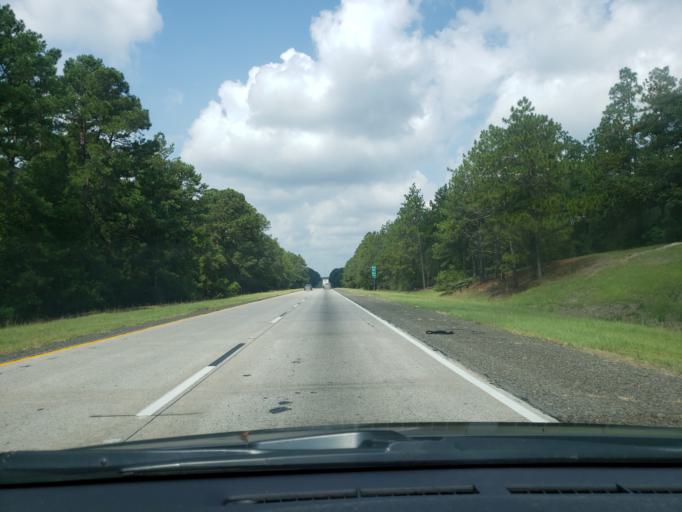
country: US
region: Georgia
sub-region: Treutlen County
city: Soperton
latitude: 32.4343
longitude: -82.6297
